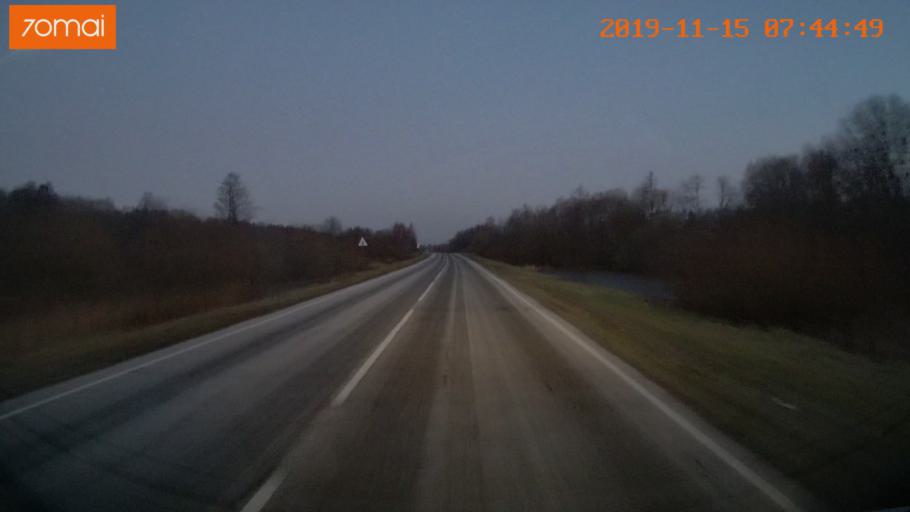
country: RU
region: Vologda
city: Sheksna
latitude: 58.8174
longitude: 38.3076
